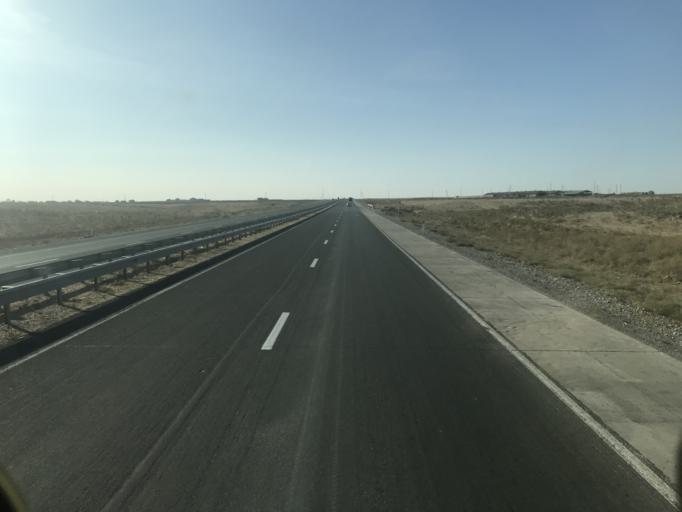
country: KZ
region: Ongtustik Qazaqstan
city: Temirlanovka
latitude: 42.5248
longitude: 69.3787
